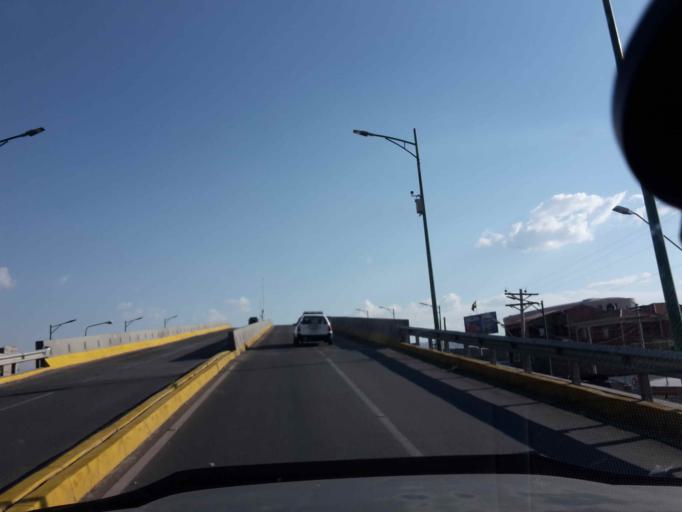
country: BO
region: Cochabamba
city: Cochabamba
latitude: -17.3920
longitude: -66.1839
